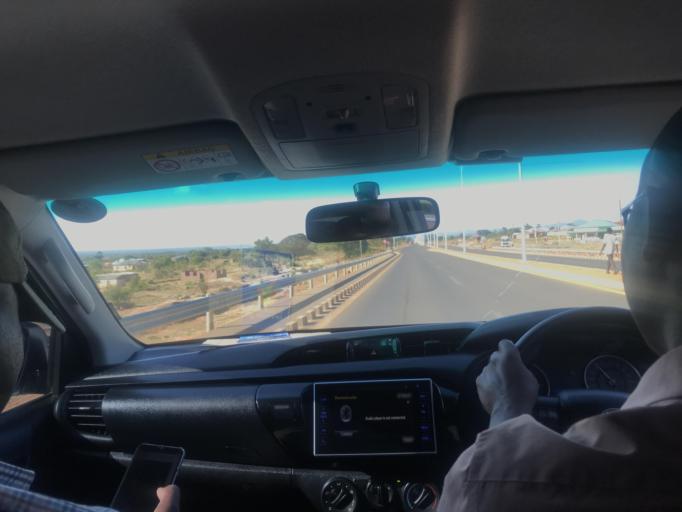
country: ZM
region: Northern
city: Mpika
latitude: -11.8288
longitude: 31.4482
